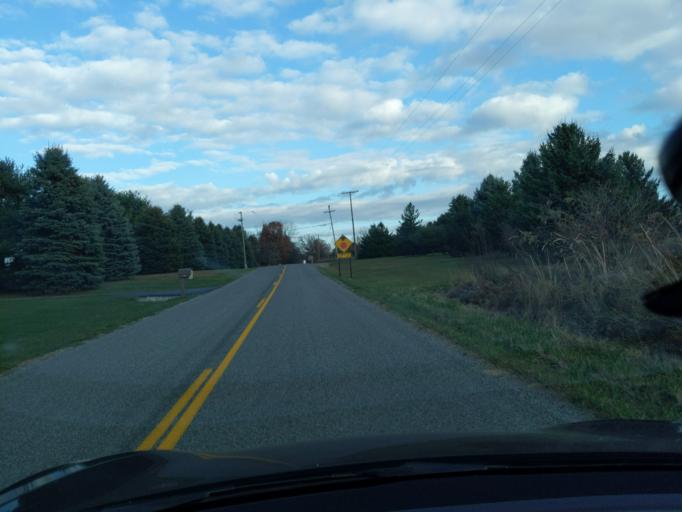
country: US
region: Michigan
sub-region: Ingham County
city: Williamston
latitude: 42.7300
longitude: -84.3189
